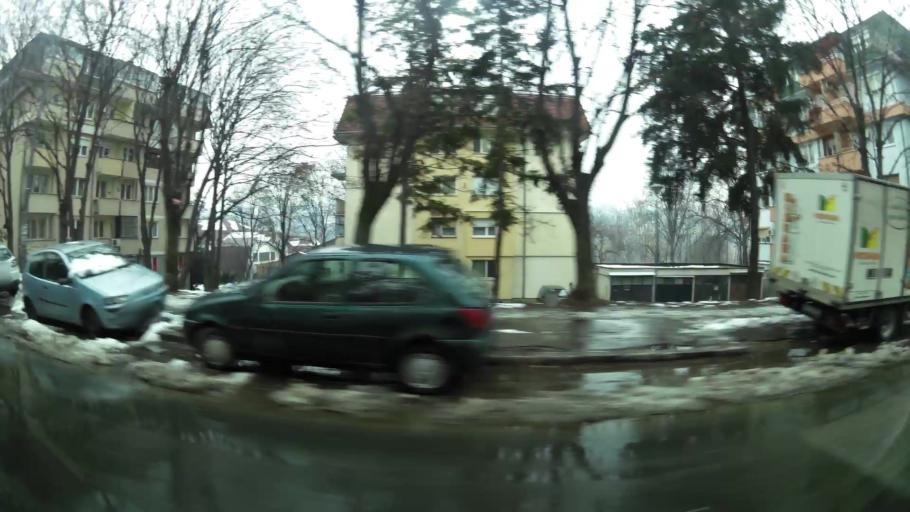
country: RS
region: Central Serbia
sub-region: Belgrade
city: Vozdovac
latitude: 44.7750
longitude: 20.4858
